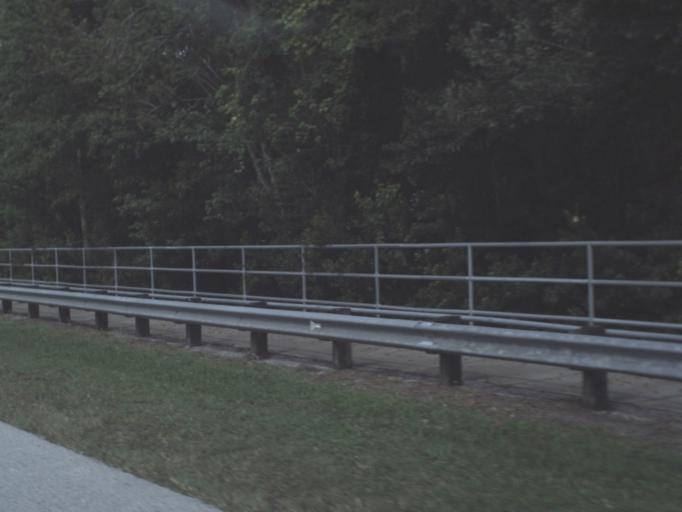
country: US
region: Florida
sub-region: Pinellas County
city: East Lake
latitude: 28.1241
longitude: -82.6962
